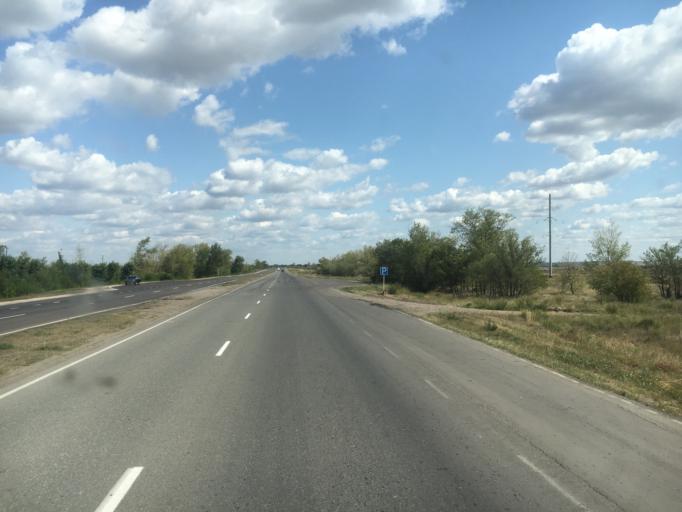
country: KZ
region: Qostanay
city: Kostanay
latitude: 53.1114
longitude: 63.5279
